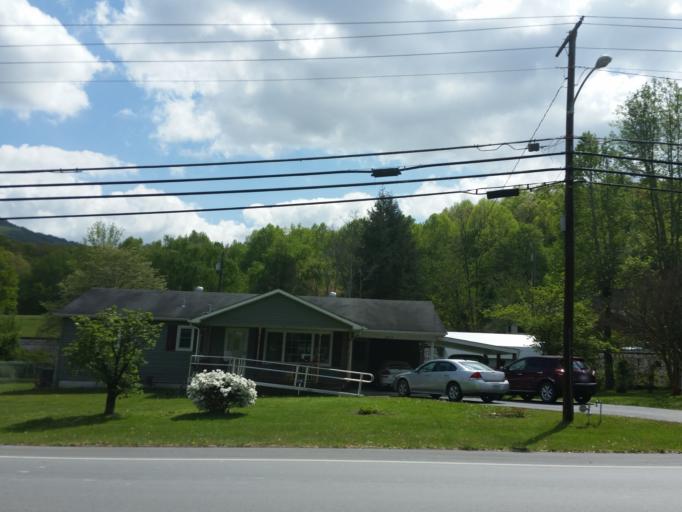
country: US
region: Kentucky
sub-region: Bell County
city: Middlesboro
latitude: 36.6097
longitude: -83.7536
